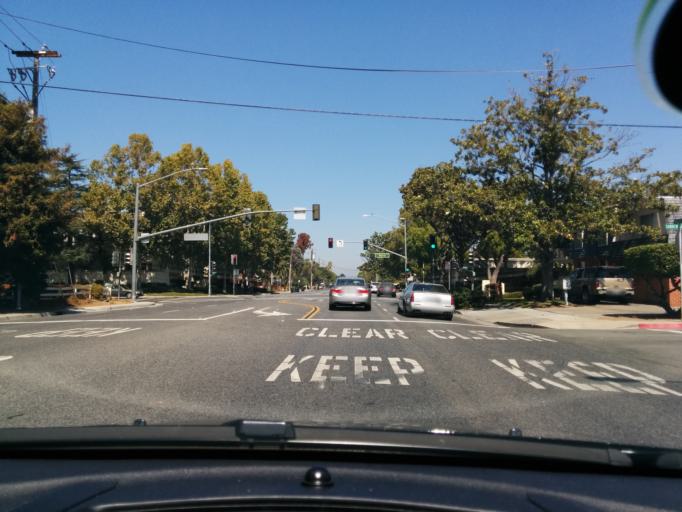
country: US
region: California
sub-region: Santa Clara County
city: Sunnyvale
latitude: 37.3556
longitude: -122.0141
